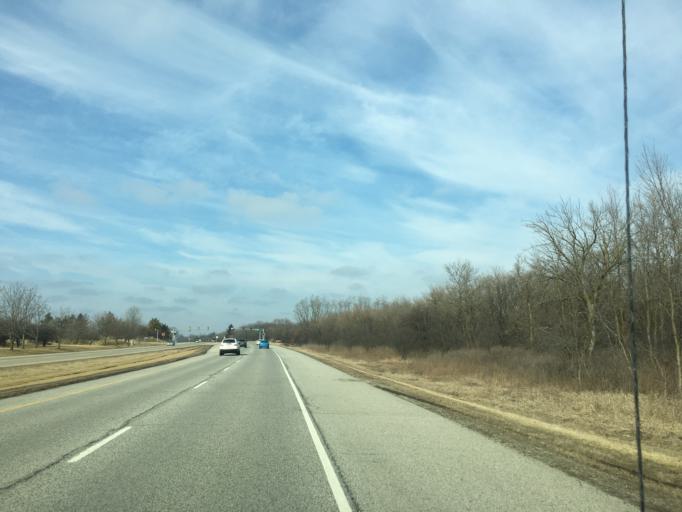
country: US
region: Illinois
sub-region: Cook County
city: Streamwood
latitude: 42.0793
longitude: -88.2063
